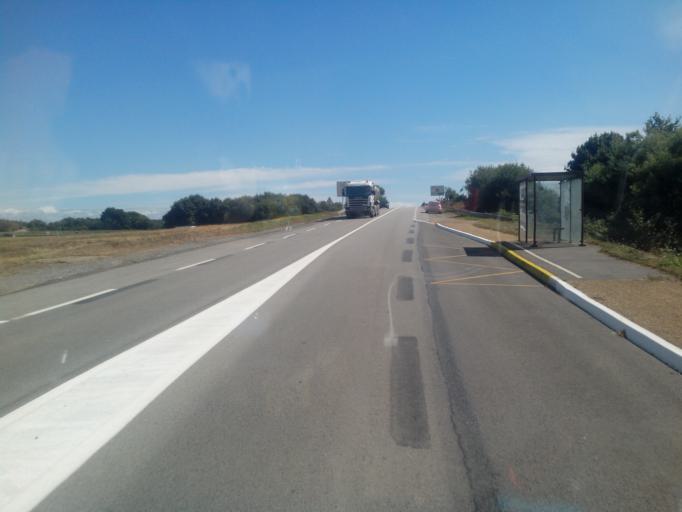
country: FR
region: Brittany
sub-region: Departement du Morbihan
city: Peaule
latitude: 47.5382
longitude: -2.3976
